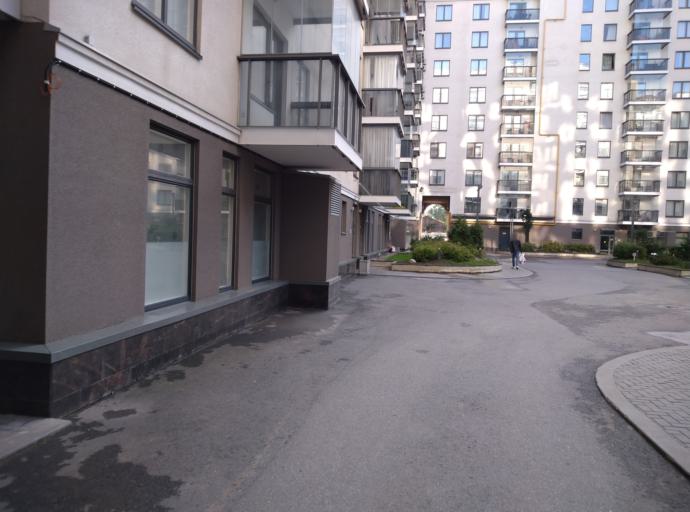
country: RU
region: St.-Petersburg
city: Admiralteisky
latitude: 59.9076
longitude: 30.3138
